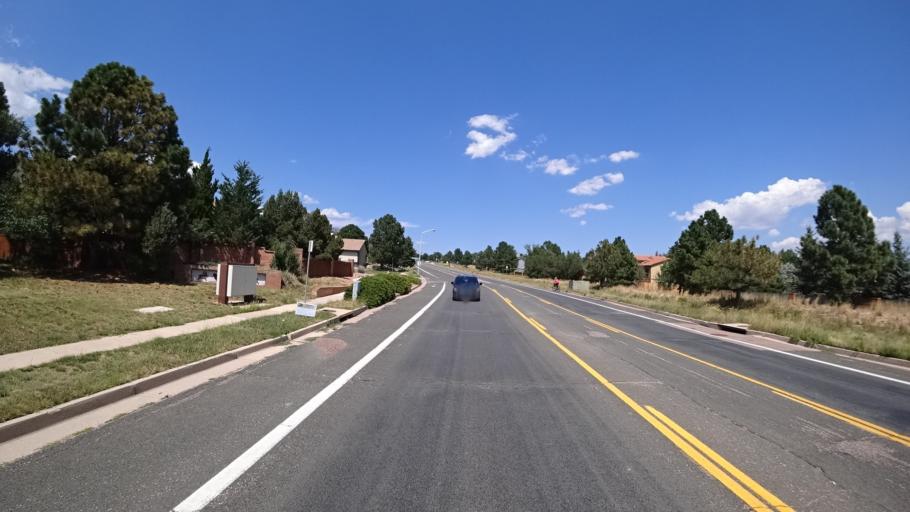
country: US
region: Colorado
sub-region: El Paso County
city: Manitou Springs
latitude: 38.9039
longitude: -104.8715
